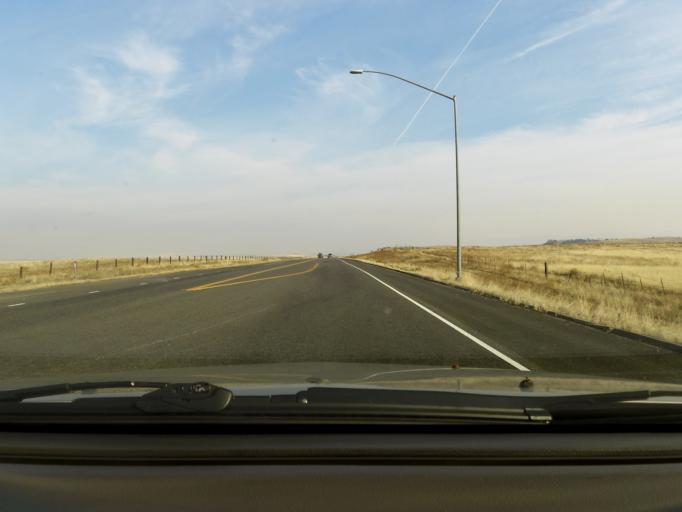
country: US
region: California
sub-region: Madera County
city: Bonadelle Ranchos-Madera Ranchos
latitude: 36.9668
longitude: -119.7940
